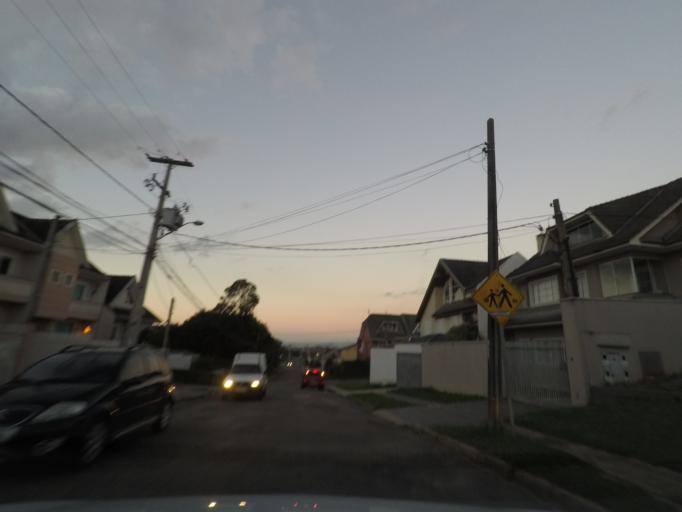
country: BR
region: Parana
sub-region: Sao Jose Dos Pinhais
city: Sao Jose dos Pinhais
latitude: -25.5007
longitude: -49.2660
